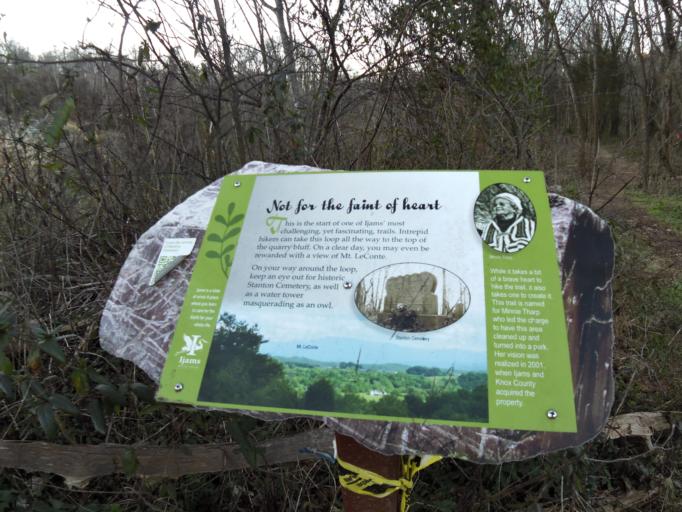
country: US
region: Tennessee
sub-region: Knox County
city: Knoxville
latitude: 35.9523
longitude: -83.8656
